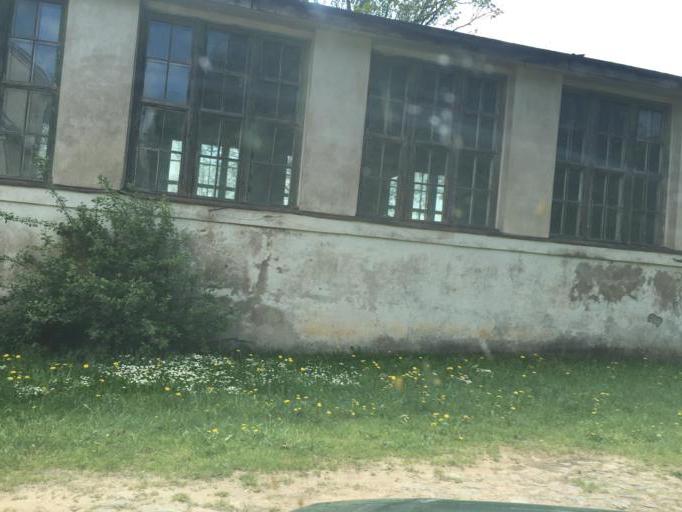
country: LV
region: Talsu Rajons
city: Valdemarpils
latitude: 57.3788
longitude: 22.6009
